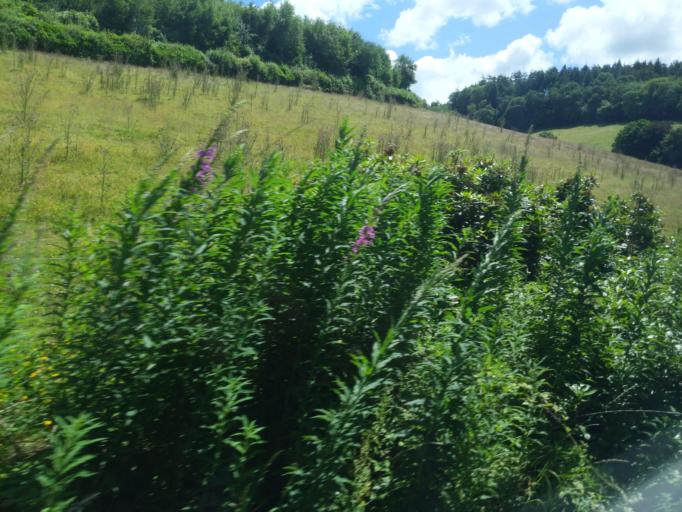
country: GB
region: England
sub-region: Cornwall
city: Lostwithiel
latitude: 50.4481
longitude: -4.6600
